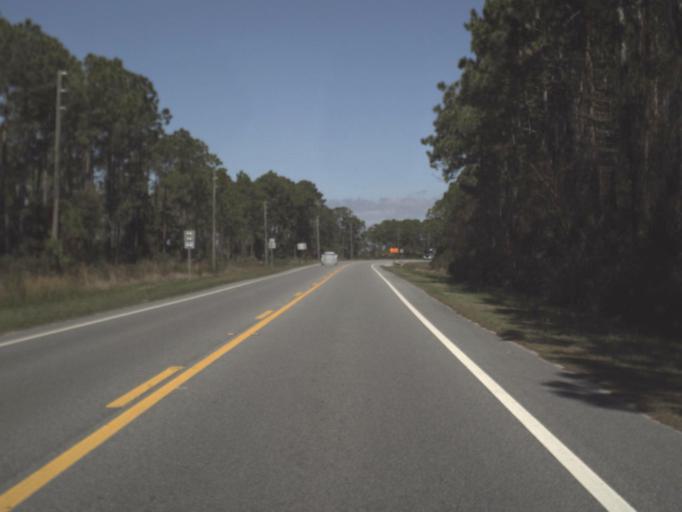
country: US
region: Florida
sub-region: Gulf County
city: Port Saint Joe
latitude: 29.7826
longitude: -85.3005
